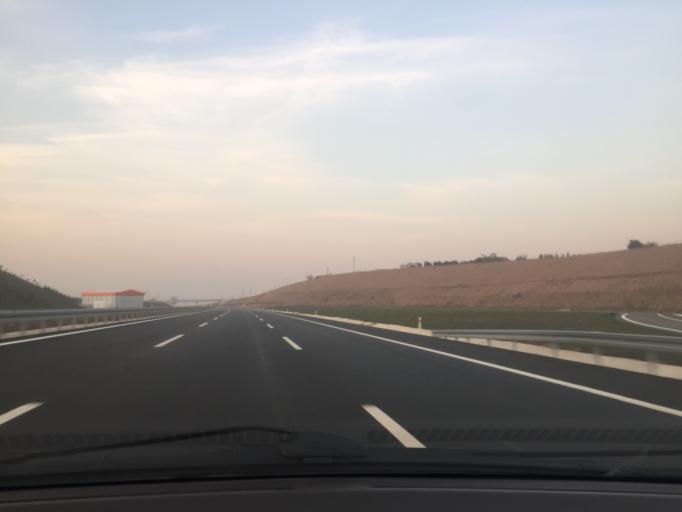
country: TR
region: Bursa
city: Karacabey
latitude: 40.2469
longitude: 28.4387
